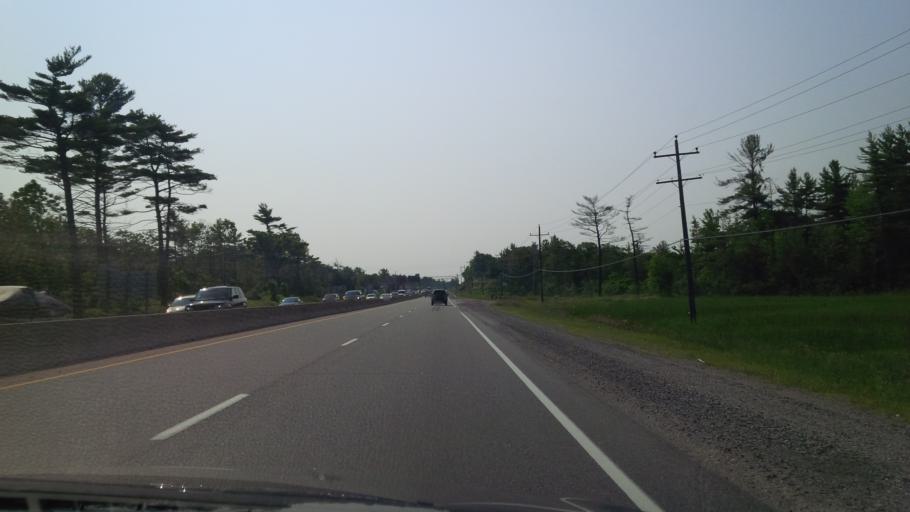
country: CA
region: Ontario
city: Gravenhurst
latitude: 44.8950
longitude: -79.3612
